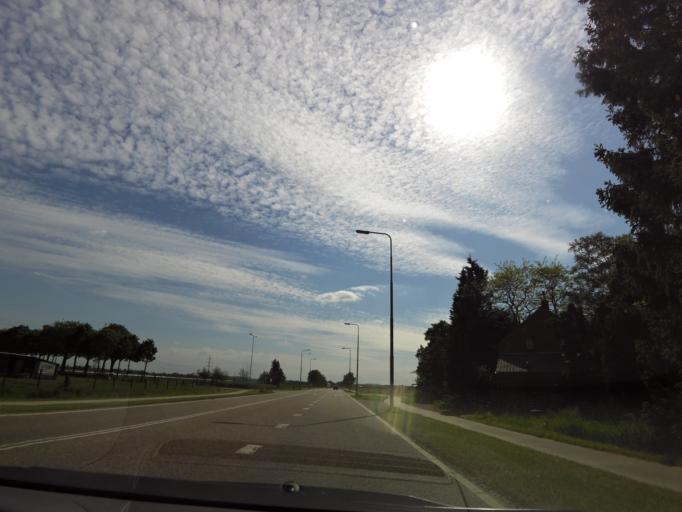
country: NL
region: Limburg
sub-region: Gemeente Echt-Susteren
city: Koningsbosch
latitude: 51.0435
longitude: 5.9515
